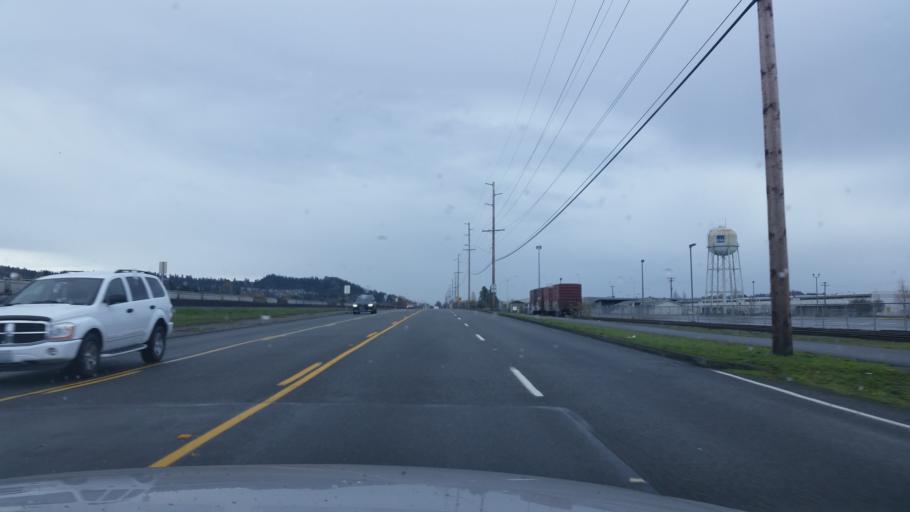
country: US
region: Washington
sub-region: King County
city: Auburn
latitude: 47.2874
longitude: -122.2317
